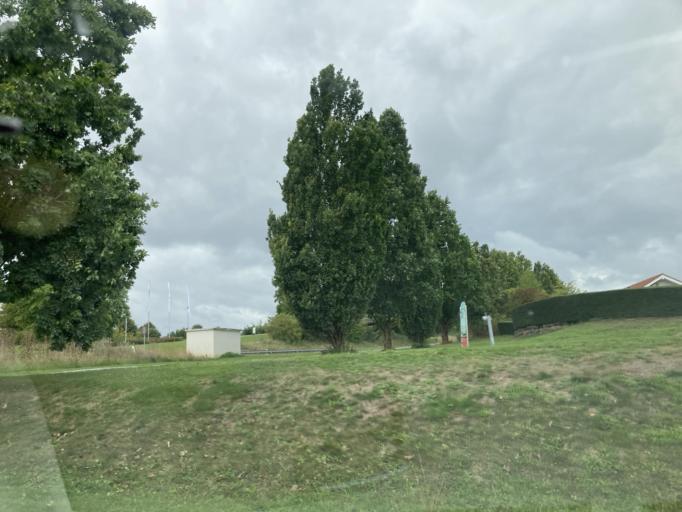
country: DE
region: Baden-Wuerttemberg
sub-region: Regierungsbezirk Stuttgart
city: Bondorf
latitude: 48.5281
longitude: 8.8065
